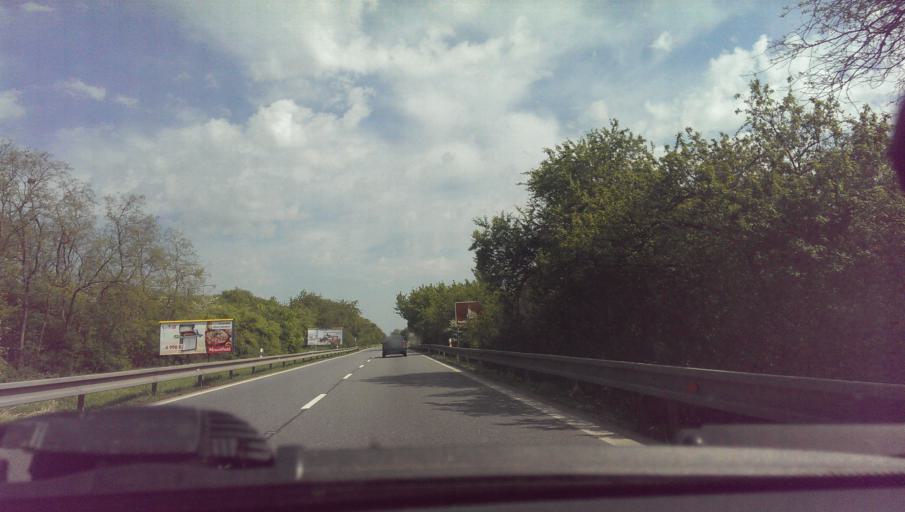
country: CZ
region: Zlin
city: Spytihnev
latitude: 49.1469
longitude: 17.5005
